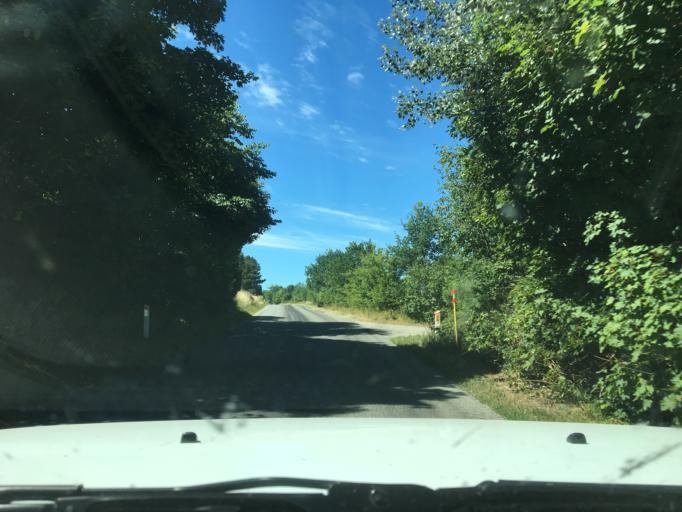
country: DK
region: Central Jutland
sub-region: Syddjurs Kommune
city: Ronde
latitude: 56.3368
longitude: 10.4048
